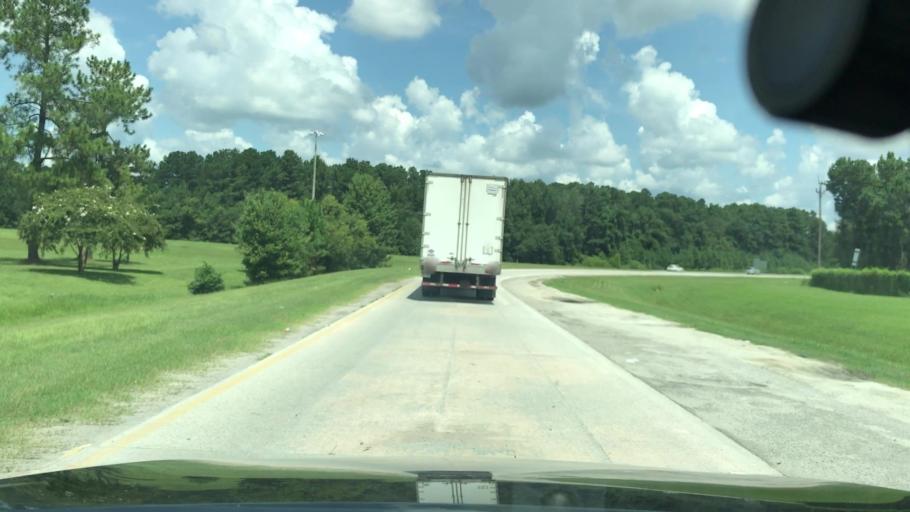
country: US
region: South Carolina
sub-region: Dorchester County
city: Saint George
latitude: 33.1961
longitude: -80.6037
